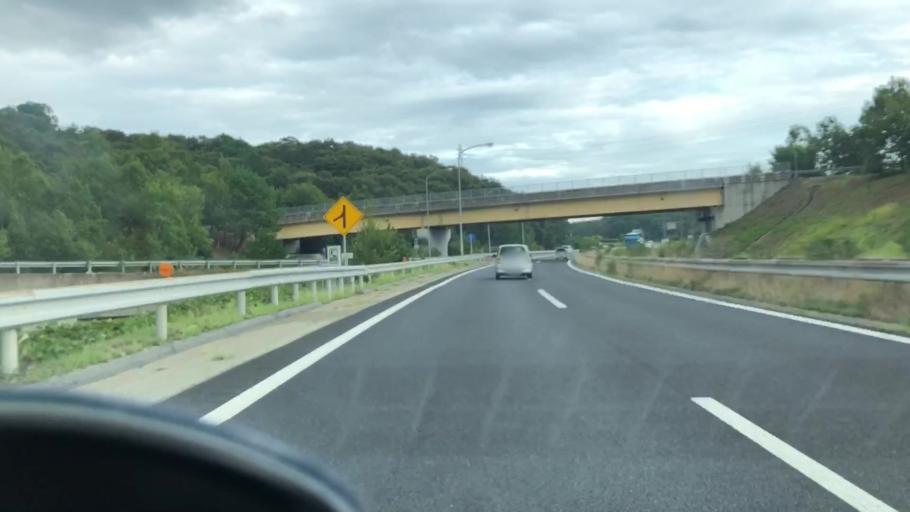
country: JP
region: Hyogo
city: Yashiro
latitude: 34.8964
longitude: 135.0790
